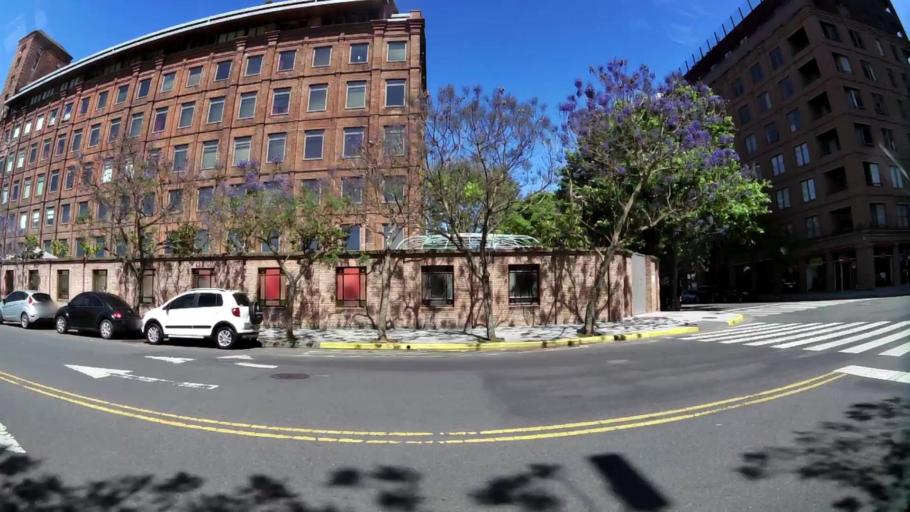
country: AR
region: Buenos Aires F.D.
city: Buenos Aires
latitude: -34.6136
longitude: -58.3613
